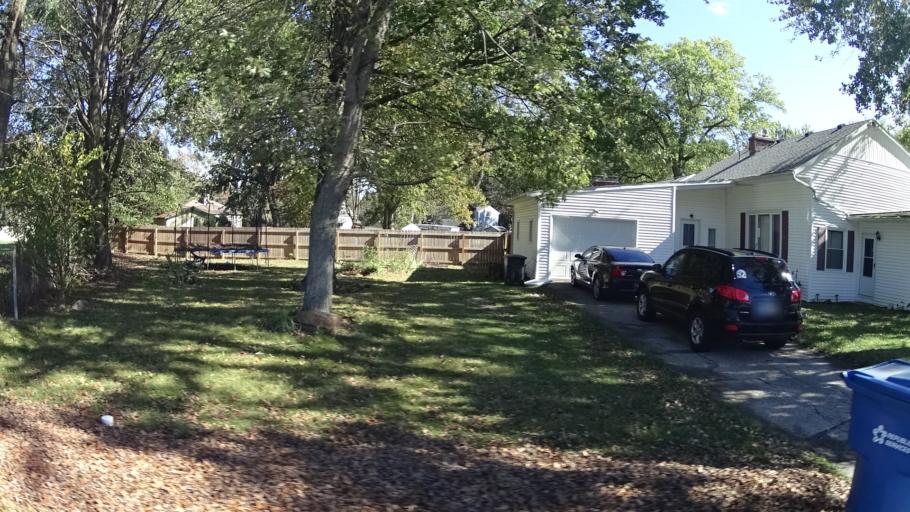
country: US
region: Ohio
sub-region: Lorain County
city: Elyria
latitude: 41.3367
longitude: -82.0902
